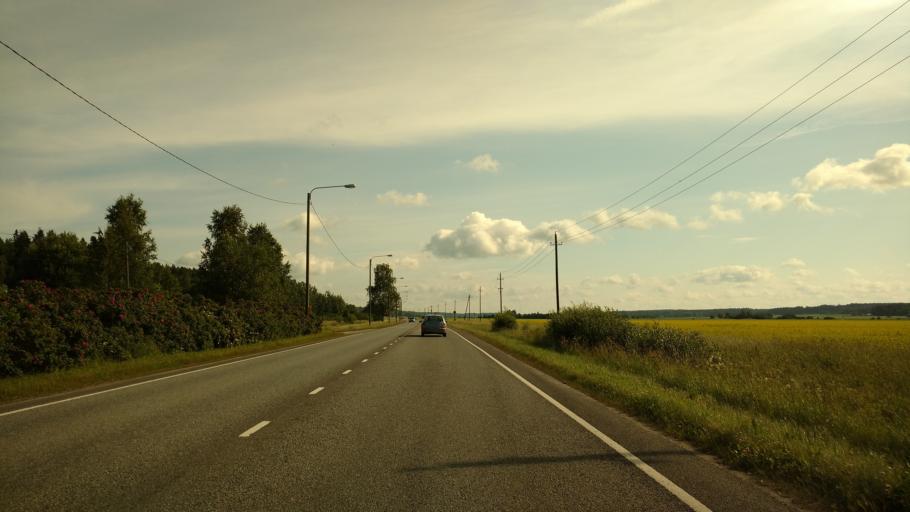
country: FI
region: Varsinais-Suomi
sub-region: Salo
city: Salo
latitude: 60.4032
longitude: 23.1479
